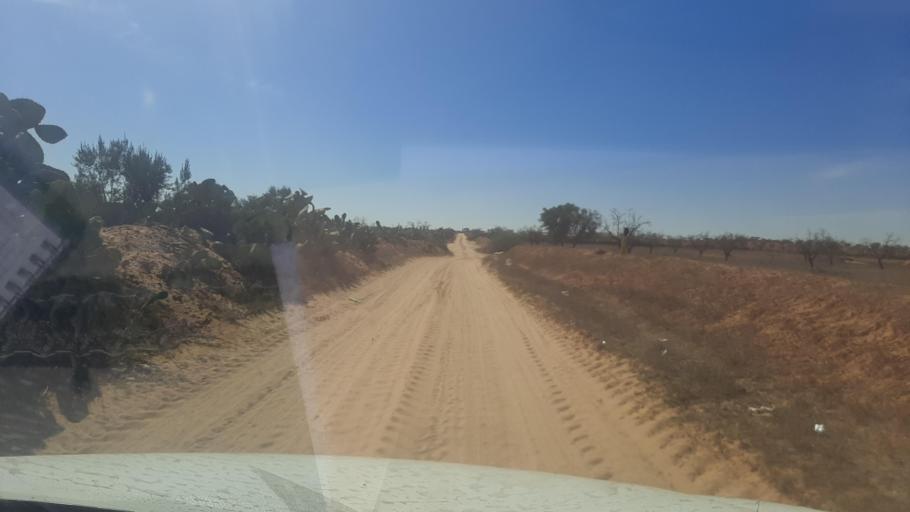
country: TN
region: Safaqis
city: Sfax
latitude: 34.8394
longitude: 10.5591
